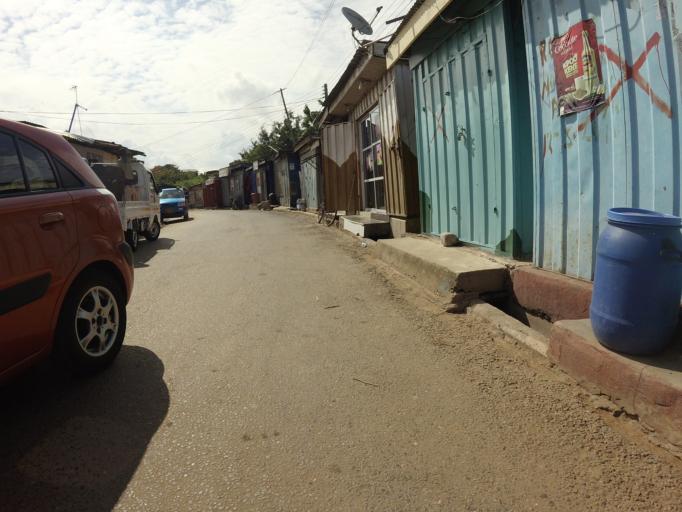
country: GH
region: Greater Accra
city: Accra
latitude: 5.5942
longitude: -0.1903
